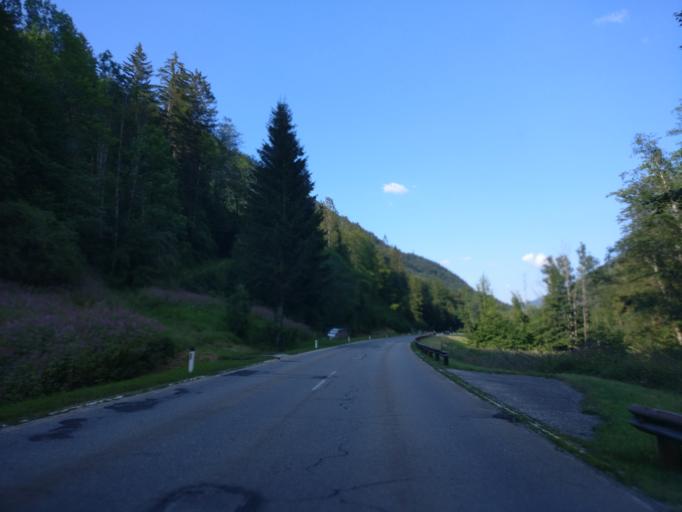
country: AT
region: Styria
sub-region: Politischer Bezirk Liezen
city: Palfau
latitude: 47.7235
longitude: 14.8490
